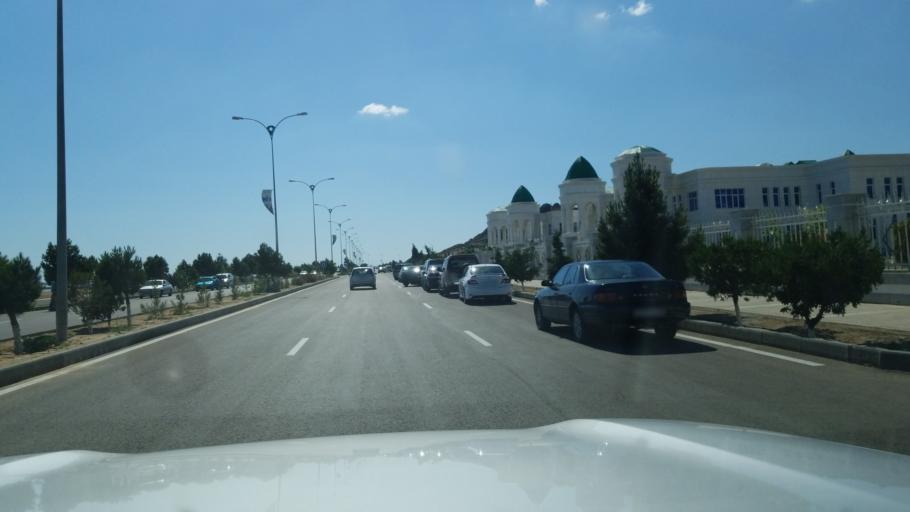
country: TM
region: Balkan
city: Turkmenbasy
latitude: 39.9905
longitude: 52.9837
